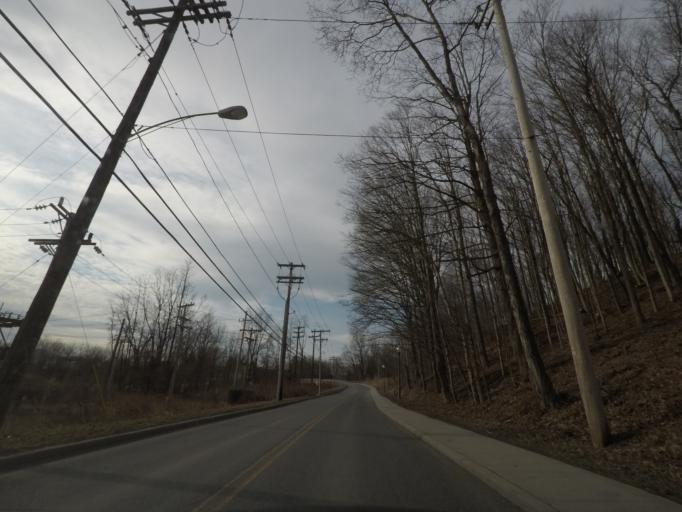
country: US
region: New York
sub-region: Rensselaer County
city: Hoosick Falls
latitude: 42.9044
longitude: -73.3535
